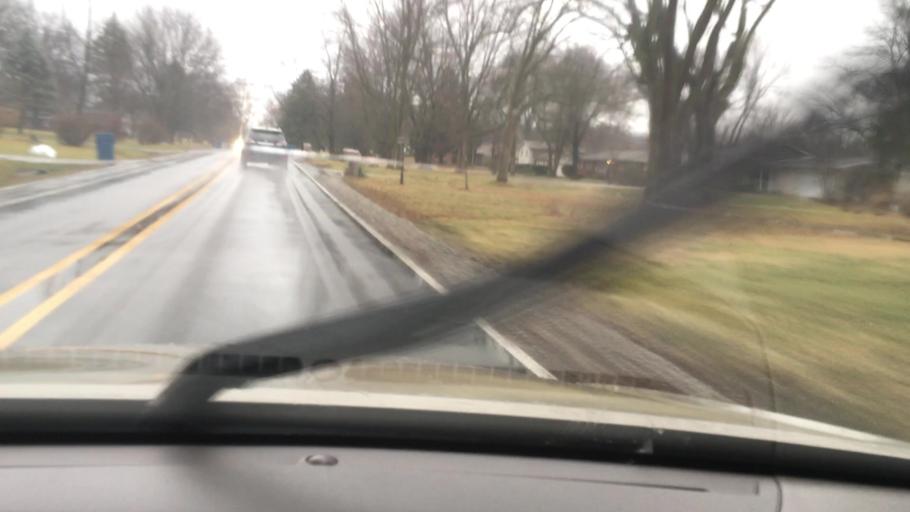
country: US
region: Indiana
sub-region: Marion County
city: Broad Ripple
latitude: 39.8832
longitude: -86.0865
